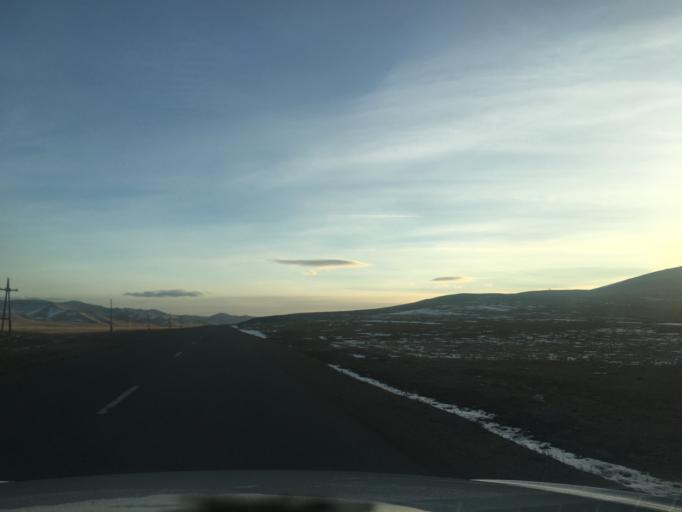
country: MN
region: Central Aimak
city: Mandal
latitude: 48.1835
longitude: 106.7033
